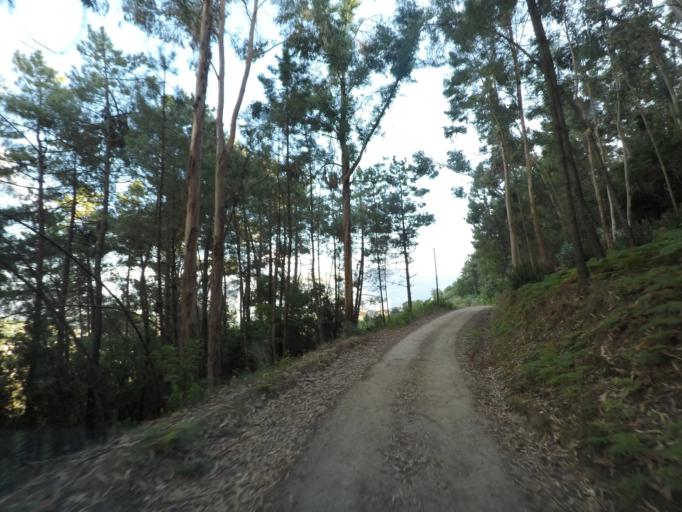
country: PT
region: Vila Real
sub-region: Mesao Frio
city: Mesao Frio
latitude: 41.1686
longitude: -7.9045
